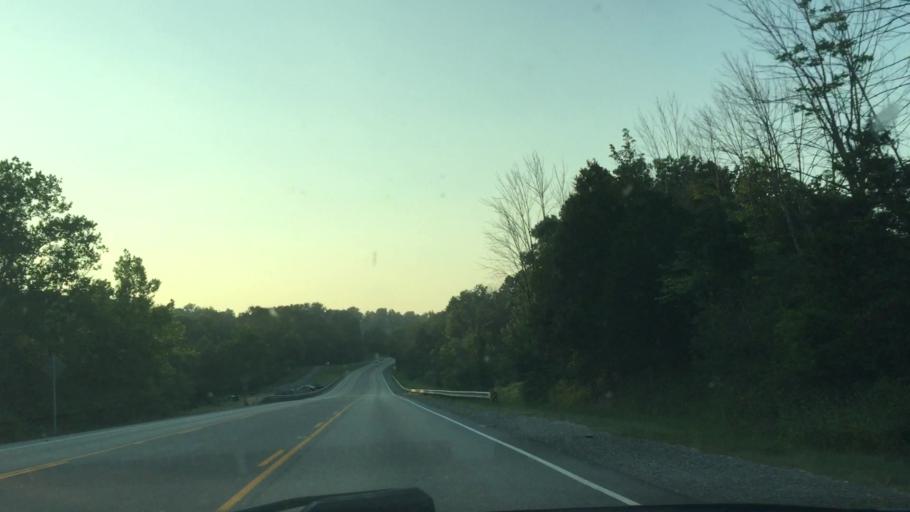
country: US
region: Kentucky
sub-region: Carroll County
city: Carrollton
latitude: 38.6685
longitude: -85.1450
